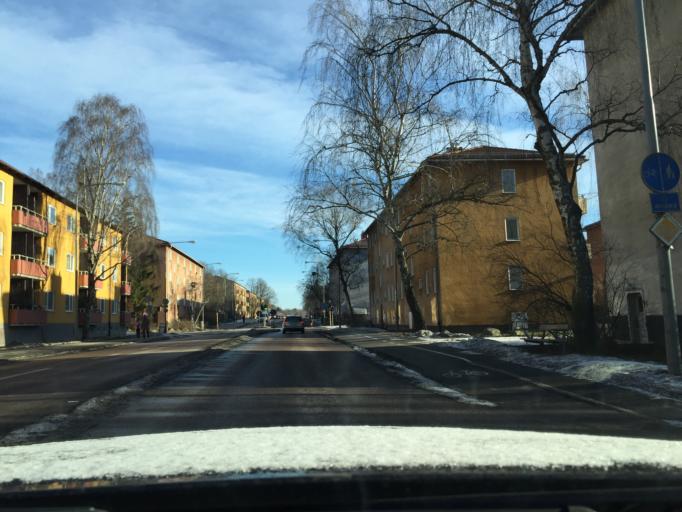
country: SE
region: Stockholm
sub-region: Stockholms Kommun
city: Bromma
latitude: 59.3407
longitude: 17.9434
